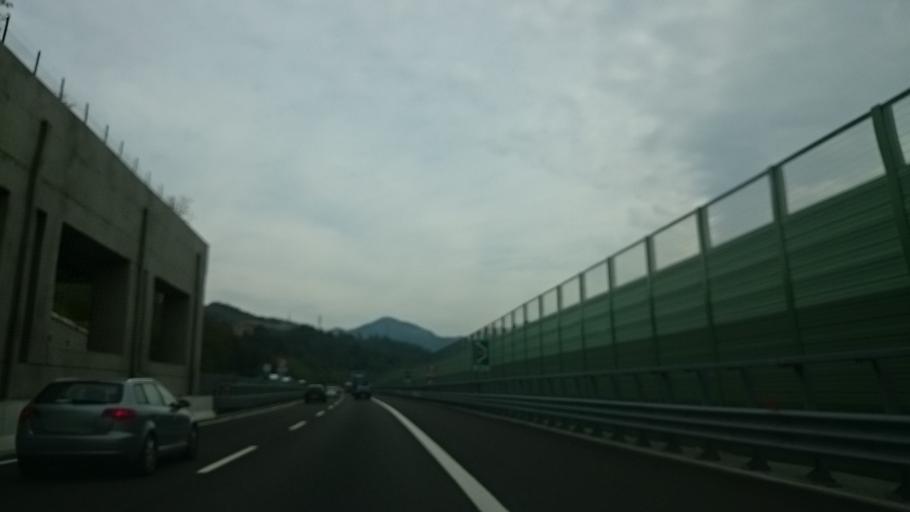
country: IT
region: Emilia-Romagna
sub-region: Provincia di Bologna
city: Grizzana
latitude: 44.2765
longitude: 11.1957
